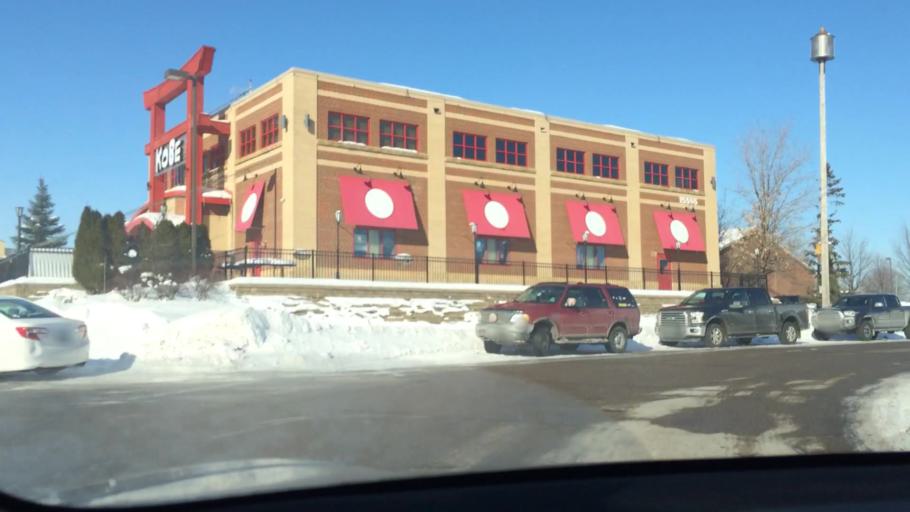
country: US
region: Minnesota
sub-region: Hennepin County
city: Plymouth
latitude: 45.0192
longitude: -93.4786
